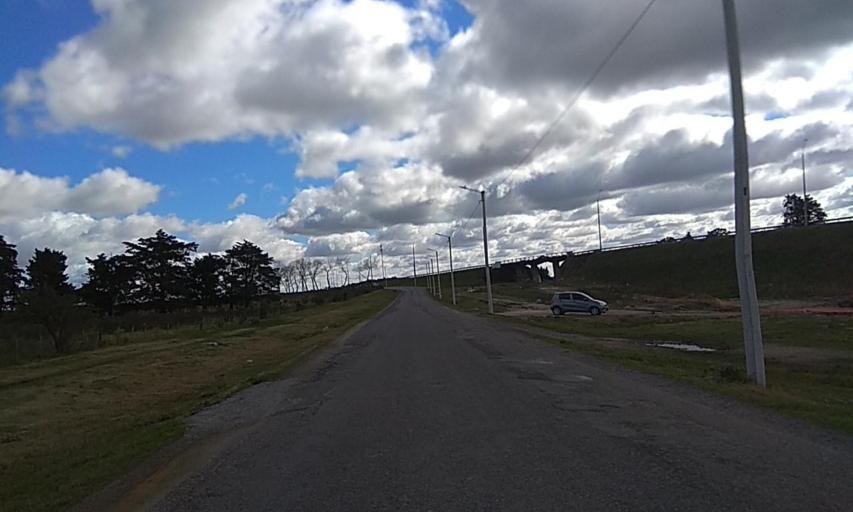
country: UY
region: Florida
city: Florida
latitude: -34.0783
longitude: -56.2299
